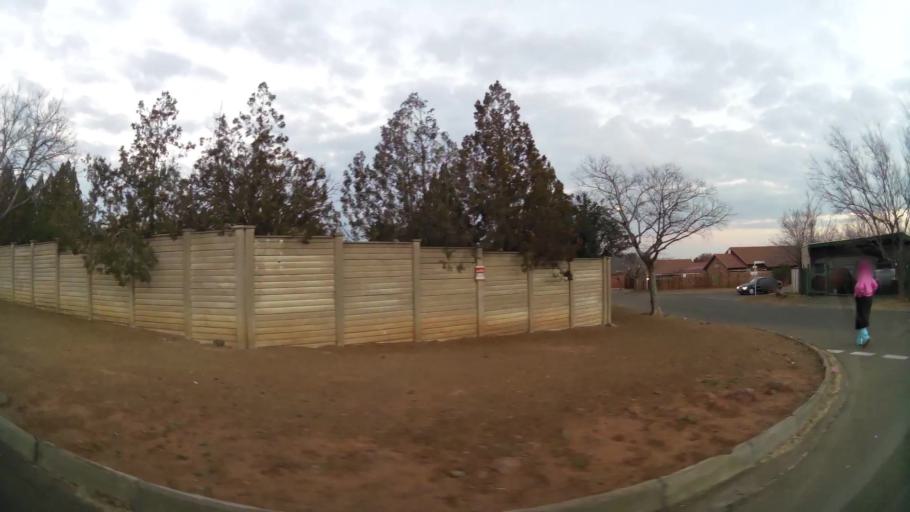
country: ZA
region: Orange Free State
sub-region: Mangaung Metropolitan Municipality
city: Bloemfontein
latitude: -29.1647
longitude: 26.1958
